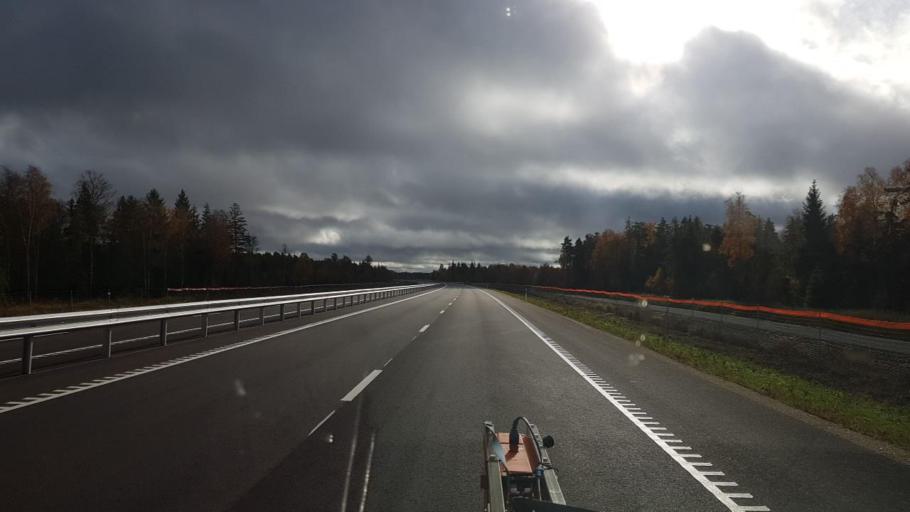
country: EE
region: Jaervamaa
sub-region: Paide linn
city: Paide
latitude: 59.0138
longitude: 25.5543
